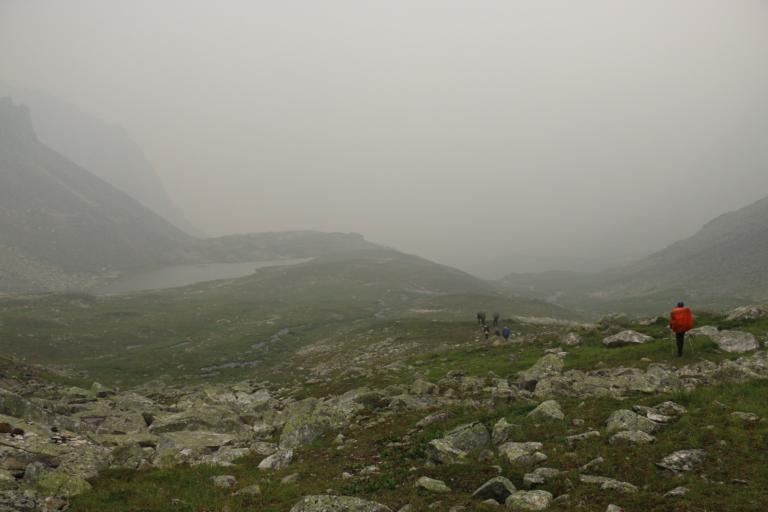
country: RU
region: Respublika Buryatiya
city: Kichera
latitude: 56.2378
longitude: 110.8610
